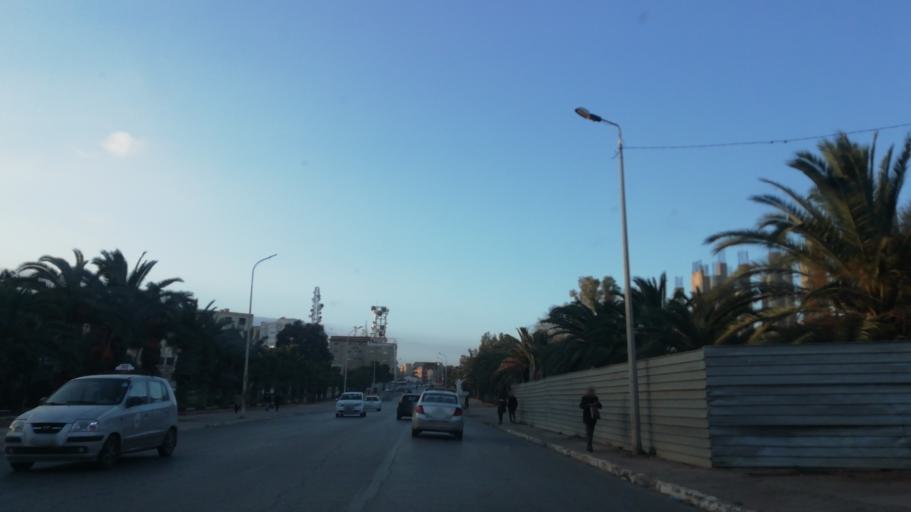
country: DZ
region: Oran
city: Oran
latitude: 35.6718
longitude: -0.6583
